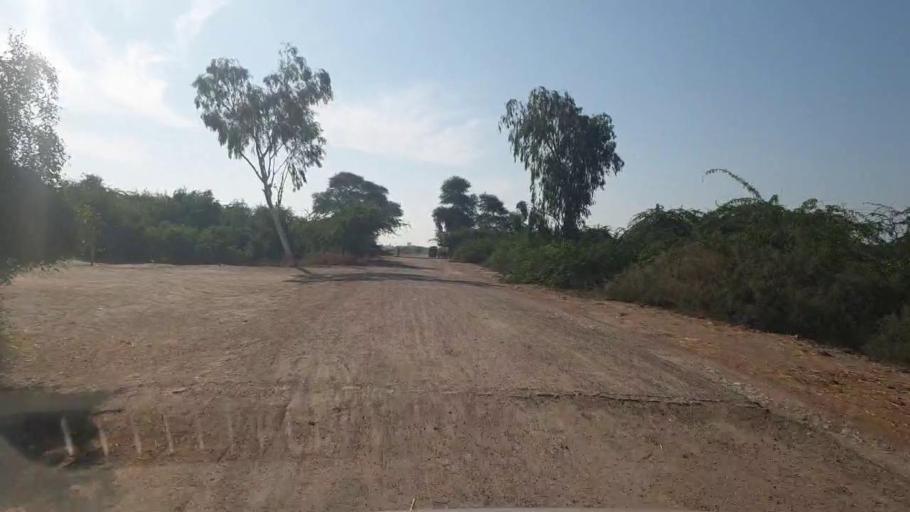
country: PK
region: Sindh
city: Rajo Khanani
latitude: 24.9632
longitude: 68.7963
